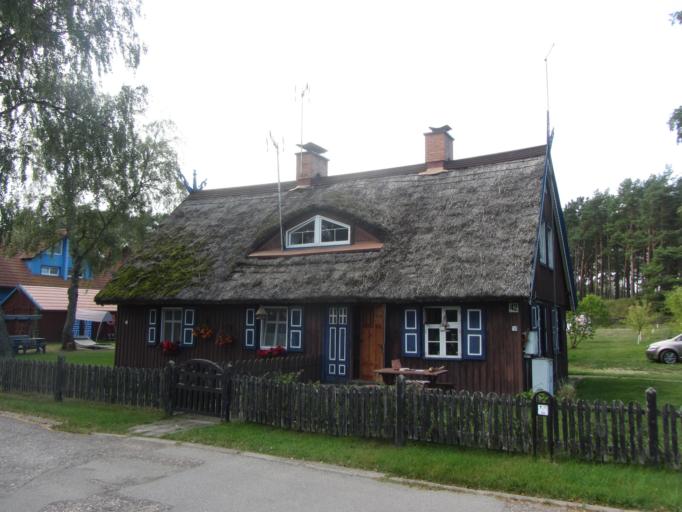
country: LT
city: Neringa
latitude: 55.4141
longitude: 21.0955
